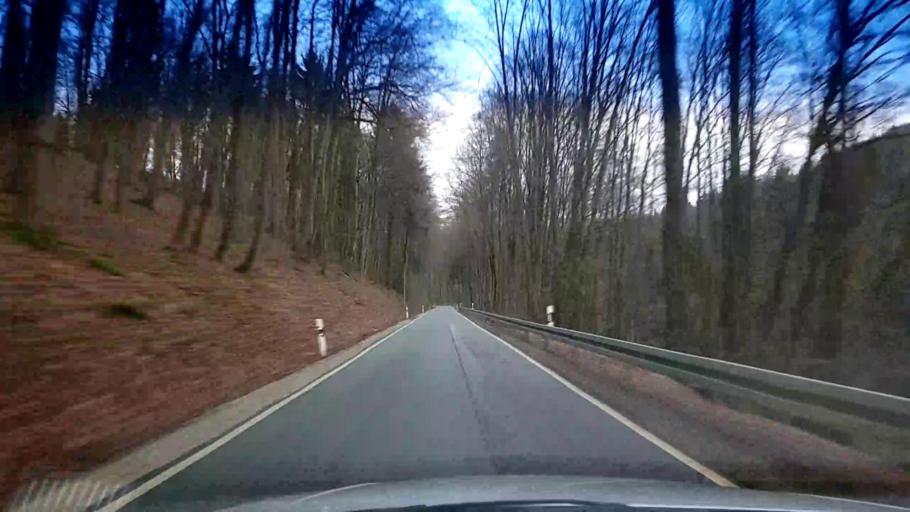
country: DE
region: Bavaria
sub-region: Upper Franconia
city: Wattendorf
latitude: 50.0588
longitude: 11.0601
